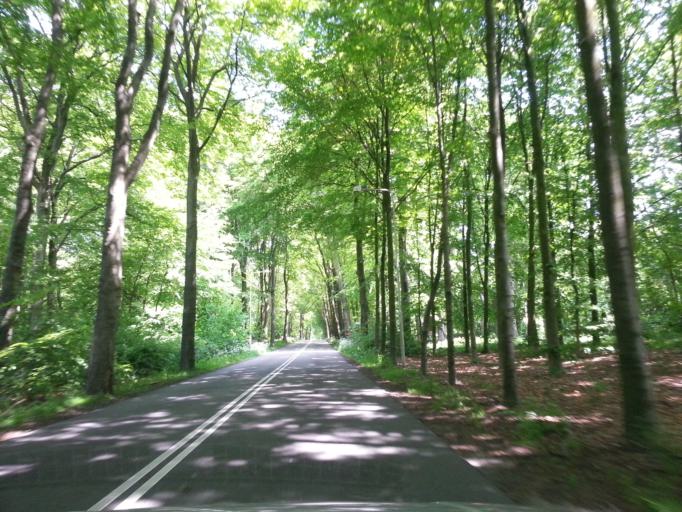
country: NL
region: Gelderland
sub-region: Gemeente Arnhem
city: Burgemeesterswijk
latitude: 52.0077
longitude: 5.9090
